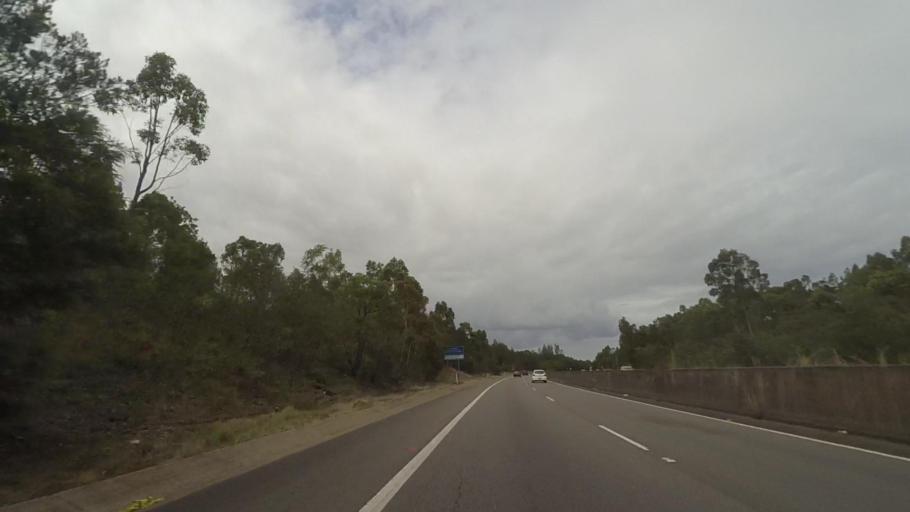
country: AU
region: New South Wales
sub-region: Port Stephens Shire
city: Raymond Terrace
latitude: -32.7492
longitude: 151.7675
